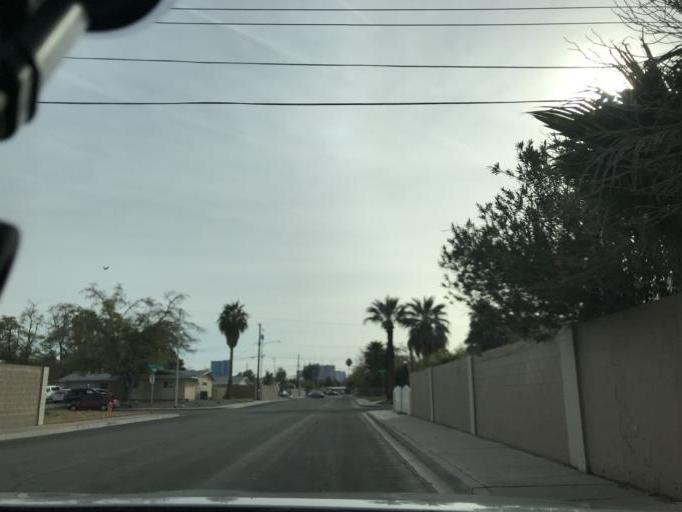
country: US
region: Nevada
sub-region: Clark County
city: Las Vegas
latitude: 36.1727
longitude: -115.1682
